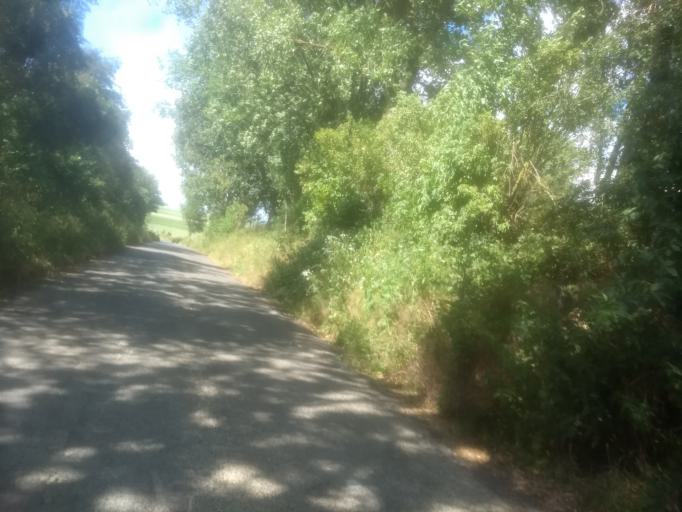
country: FR
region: Nord-Pas-de-Calais
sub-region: Departement du Pas-de-Calais
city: Tilloy-les-Mofflaines
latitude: 50.2504
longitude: 2.8237
